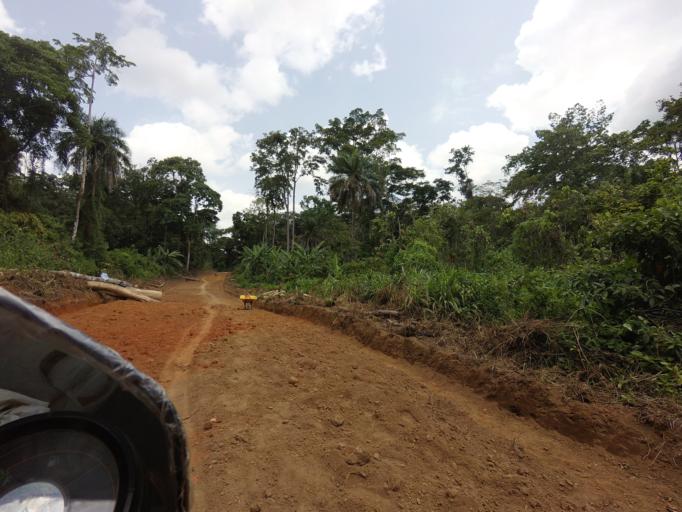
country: SL
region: Eastern Province
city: Tombu
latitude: 8.3775
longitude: -10.7085
